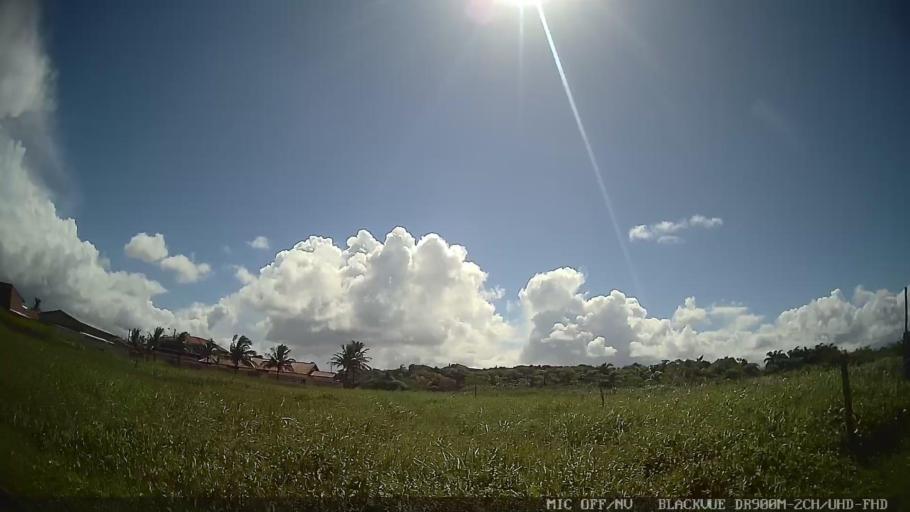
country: BR
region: Sao Paulo
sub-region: Itanhaem
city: Itanhaem
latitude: -24.2388
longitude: -46.8793
